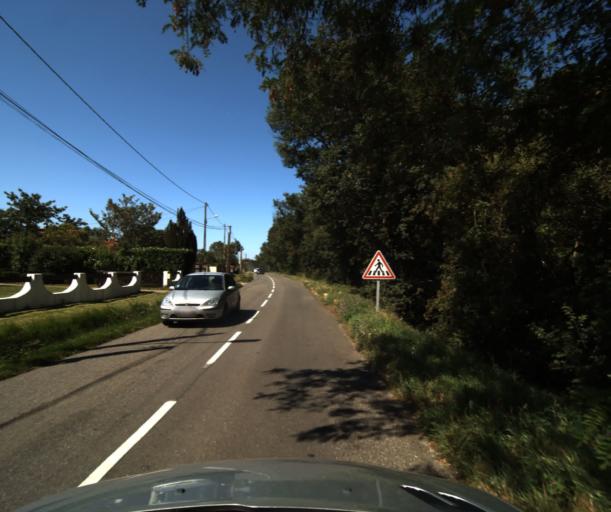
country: FR
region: Midi-Pyrenees
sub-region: Departement de la Haute-Garonne
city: Roquettes
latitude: 43.4942
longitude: 1.3554
